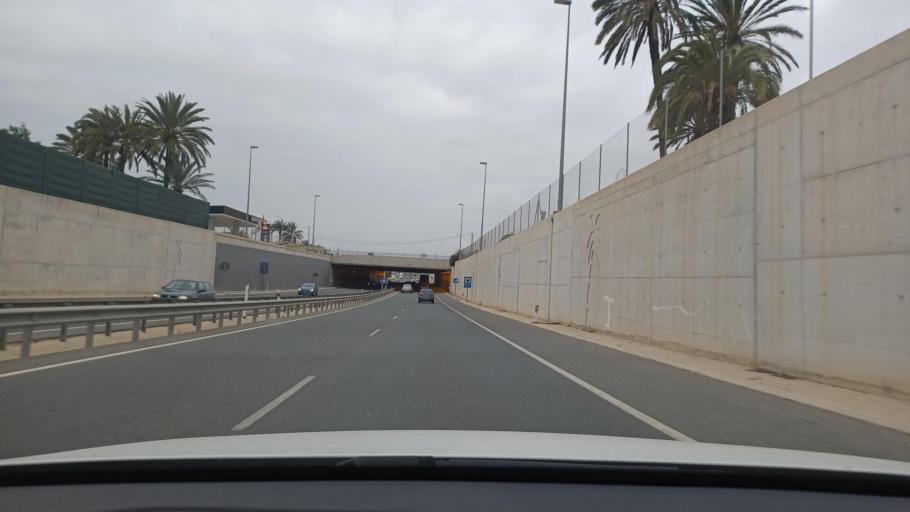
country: ES
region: Valencia
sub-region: Provincia de Alicante
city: Elche
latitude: 38.2586
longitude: -0.6771
